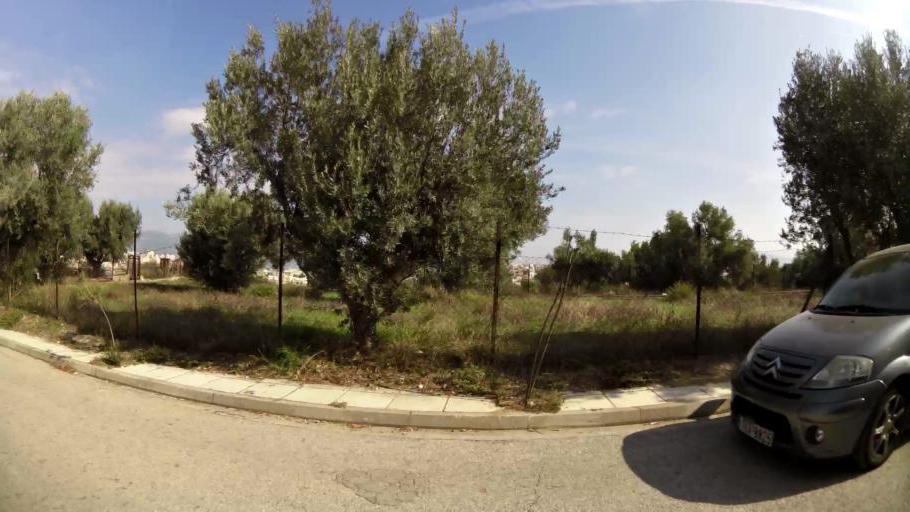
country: GR
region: Attica
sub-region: Nomarchia Athinas
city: Kamateron
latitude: 38.0514
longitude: 23.7105
